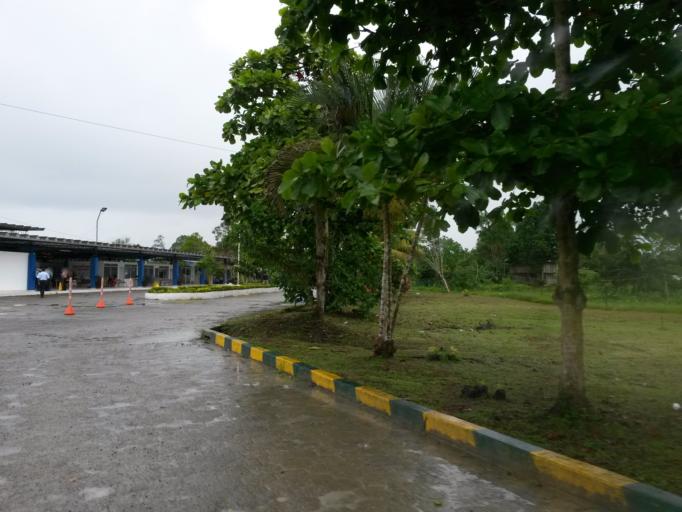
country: CO
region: Cauca
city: Guapi
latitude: 2.5745
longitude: -77.8946
